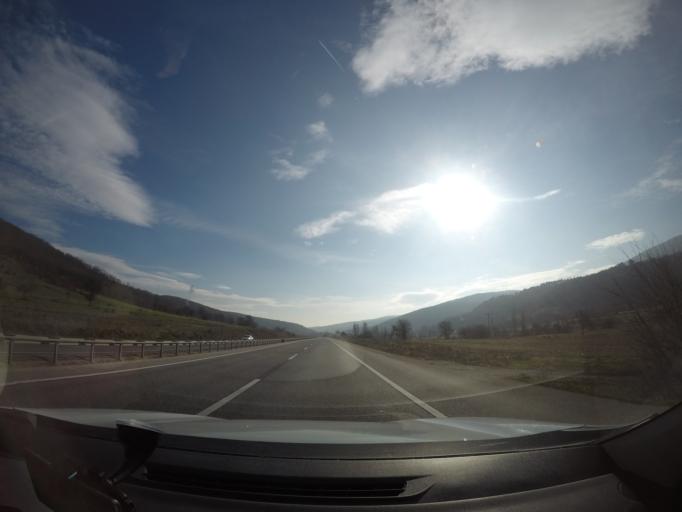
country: TR
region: Bilecik
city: Dodurga
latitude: 39.8907
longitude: 29.9081
